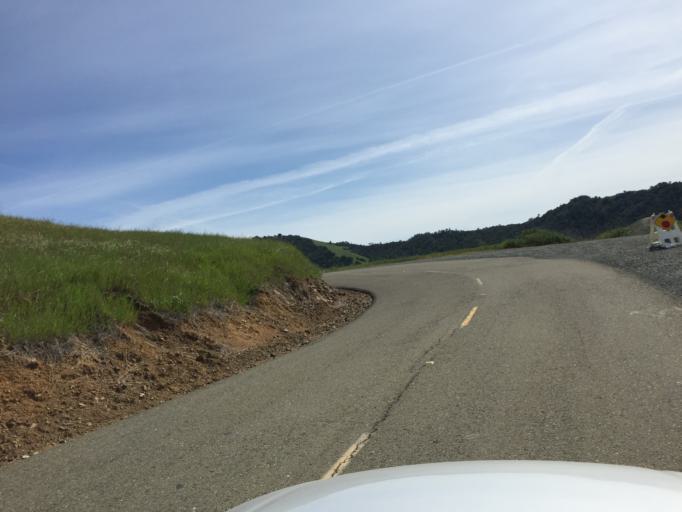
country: US
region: California
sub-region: Contra Costa County
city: Diablo
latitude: 37.8729
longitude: -121.9580
